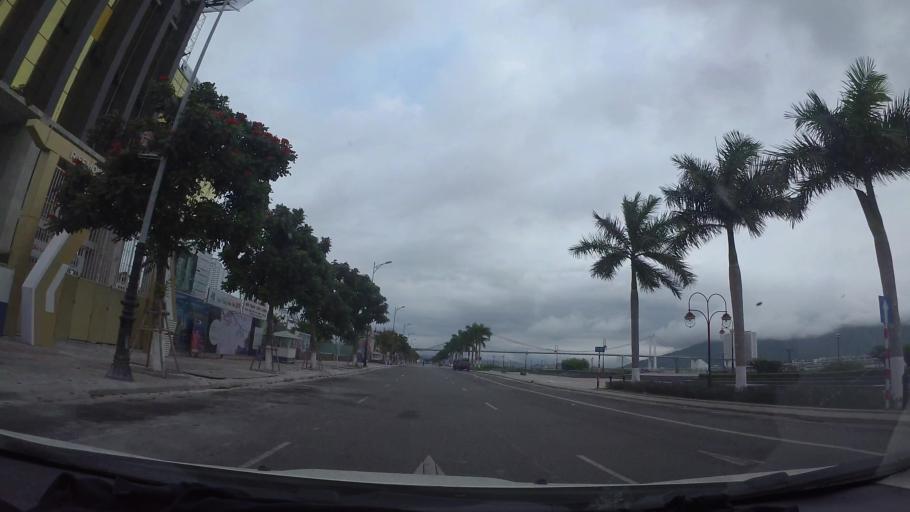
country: VN
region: Da Nang
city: Da Nang
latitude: 16.0869
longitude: 108.2215
